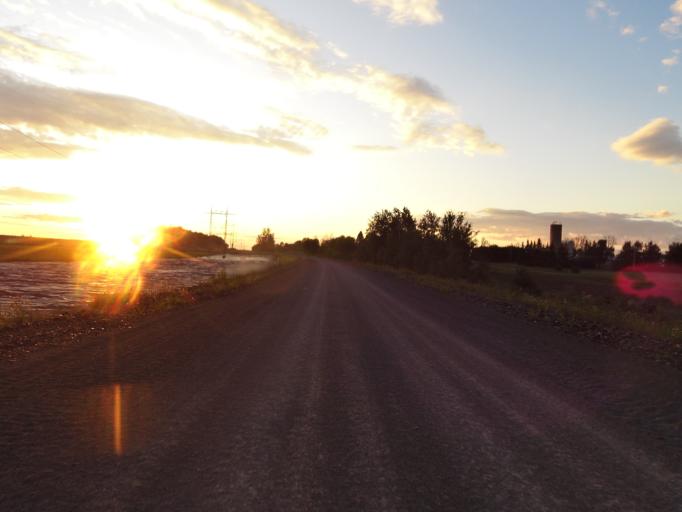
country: CA
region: Ontario
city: Arnprior
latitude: 45.4038
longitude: -76.3259
